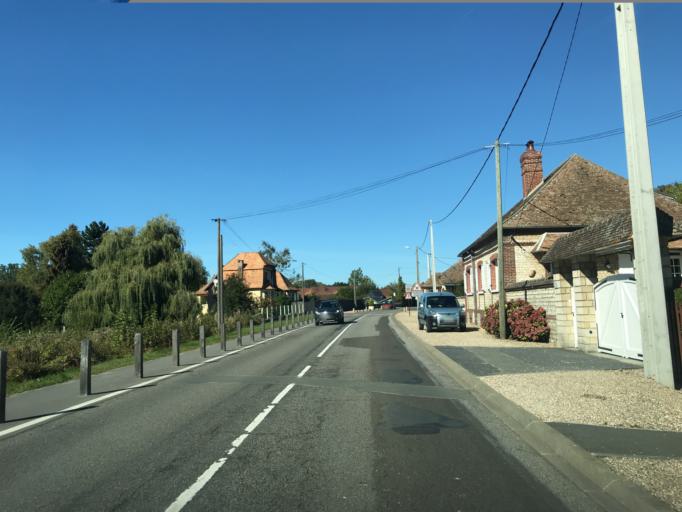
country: FR
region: Haute-Normandie
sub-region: Departement de l'Eure
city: Le Vaudreuil
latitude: 49.2514
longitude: 1.2086
